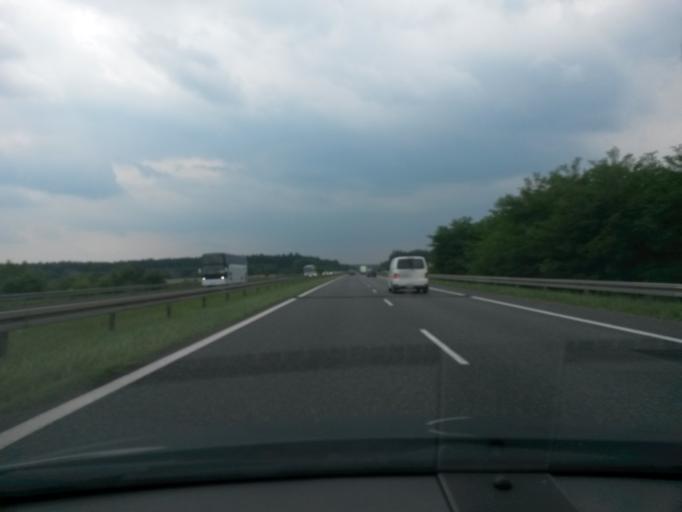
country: PL
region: Lodz Voivodeship
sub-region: Powiat radomszczanski
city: Radomsko
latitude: 51.0668
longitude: 19.3655
